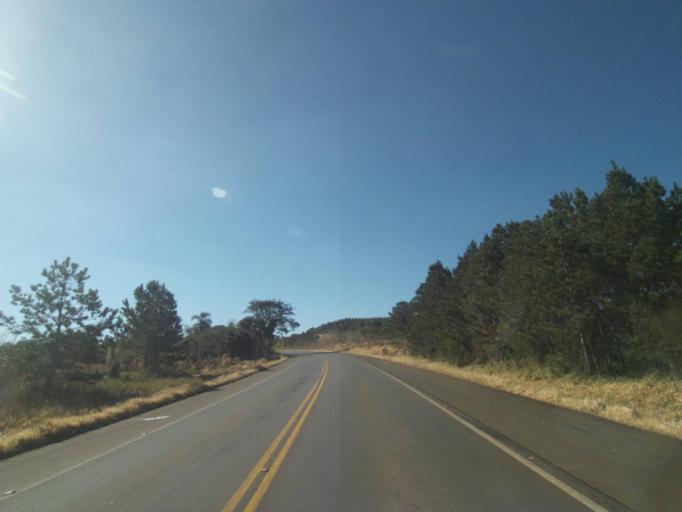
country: BR
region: Parana
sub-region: Tibagi
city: Tibagi
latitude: -24.7359
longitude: -50.4543
